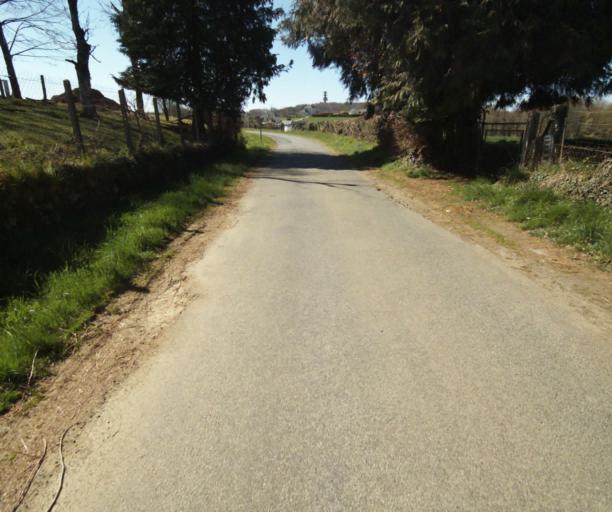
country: FR
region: Limousin
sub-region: Departement de la Correze
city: Seilhac
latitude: 45.3618
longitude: 1.7249
